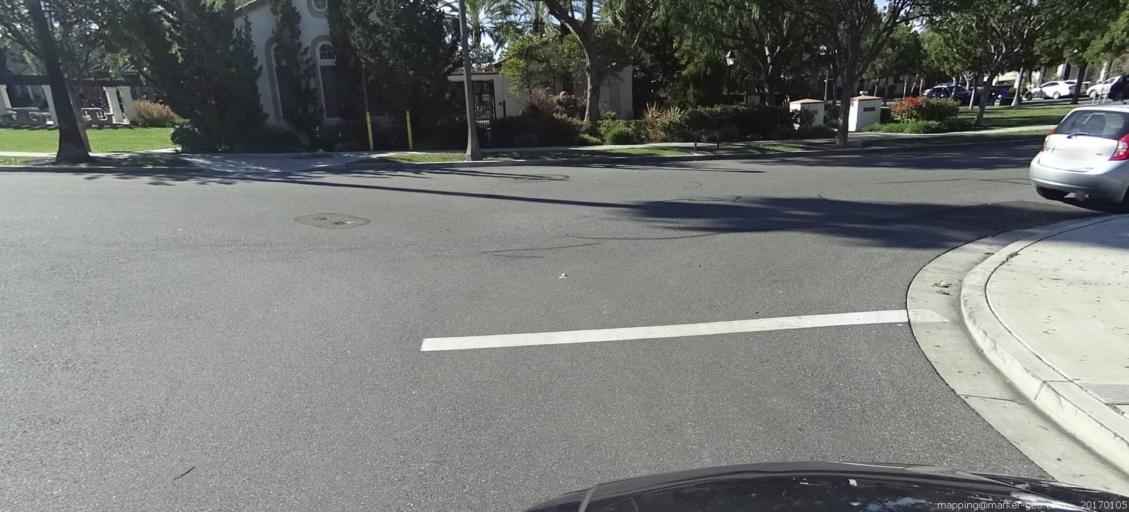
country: US
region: California
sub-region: Orange County
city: Ladera Ranch
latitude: 33.5534
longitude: -117.6327
